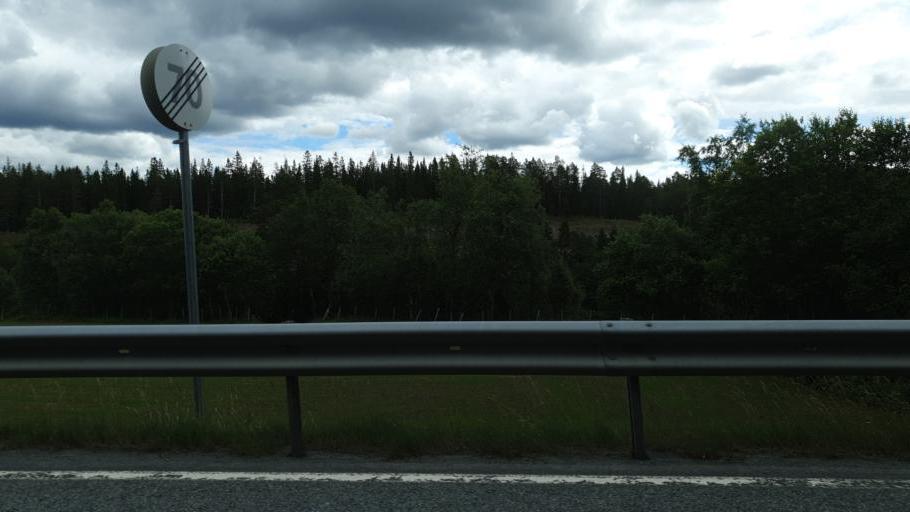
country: NO
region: Sor-Trondelag
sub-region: Rennebu
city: Berkak
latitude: 62.8943
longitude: 10.1042
